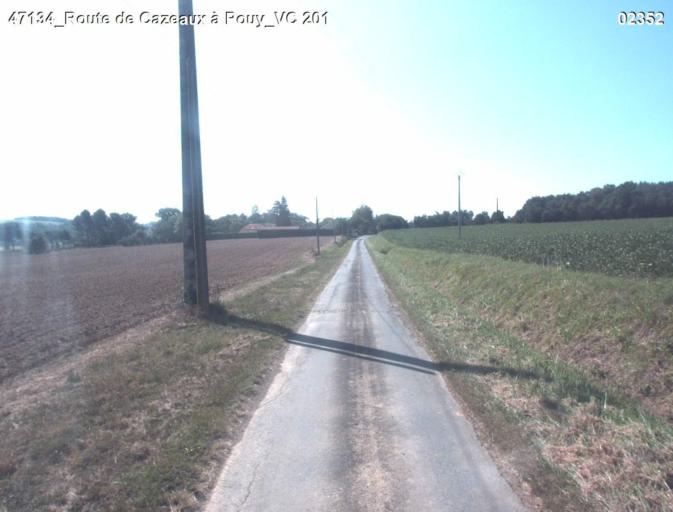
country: FR
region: Aquitaine
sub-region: Departement du Lot-et-Garonne
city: Mezin
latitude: 44.0218
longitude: 0.3131
